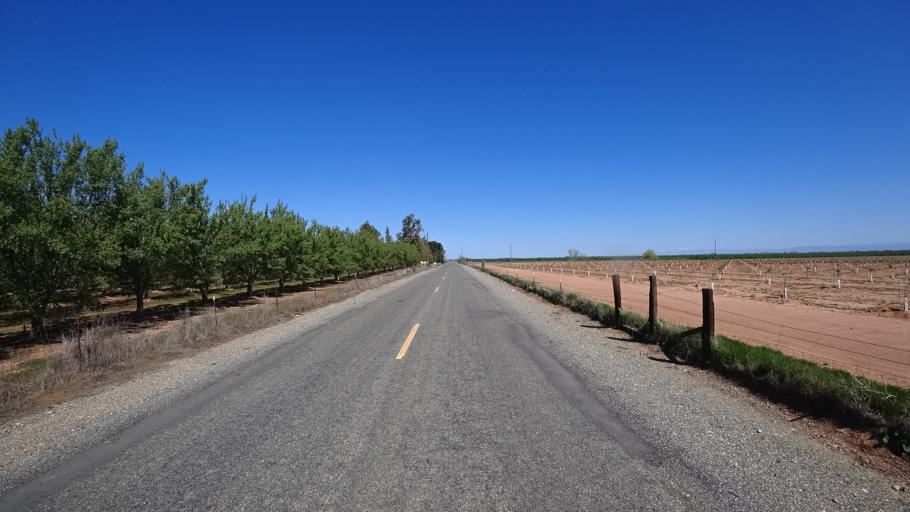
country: US
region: California
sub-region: Glenn County
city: Orland
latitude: 39.6799
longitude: -122.2531
